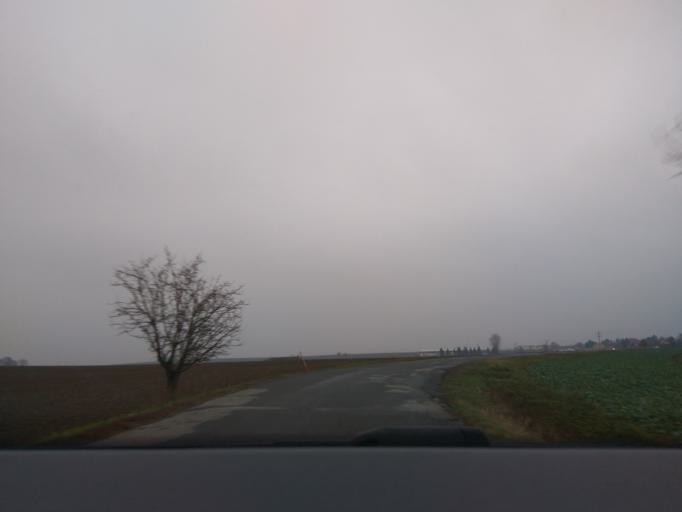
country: CZ
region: Praha
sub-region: Praha 19
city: Kbely
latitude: 50.1656
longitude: 14.5659
